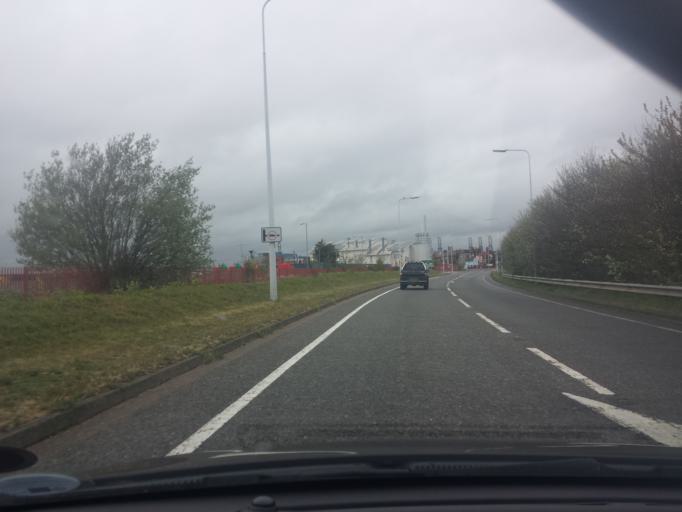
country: GB
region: England
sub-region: Essex
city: Harwich
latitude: 51.9434
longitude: 1.2838
